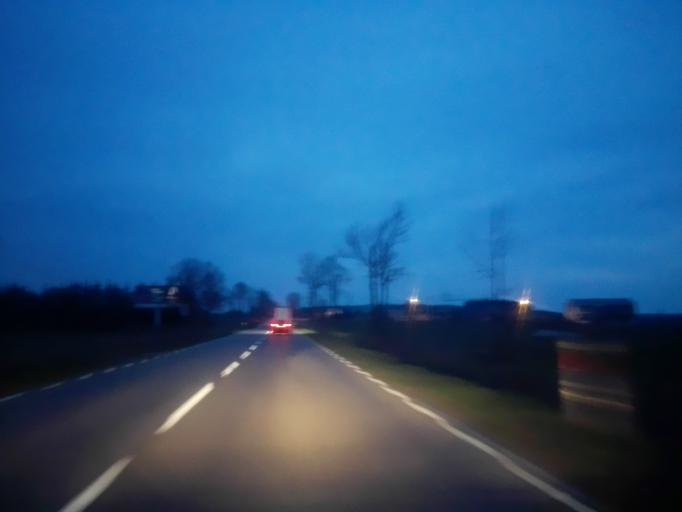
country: PL
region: Podlasie
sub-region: Lomza
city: Lomza
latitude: 53.1148
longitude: 22.0306
